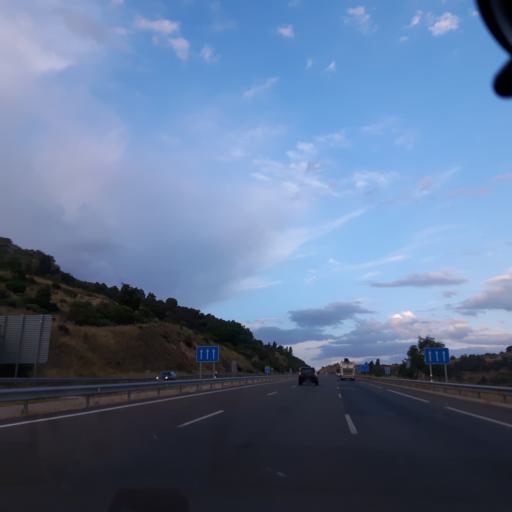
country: ES
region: Castille and Leon
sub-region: Provincia de Salamanca
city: Fresnedoso
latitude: 40.4295
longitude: -5.6976
